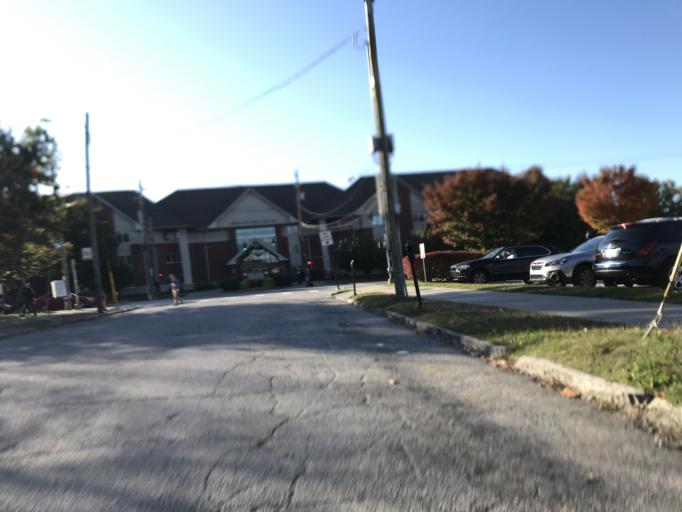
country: US
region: Kentucky
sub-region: Jefferson County
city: Louisville
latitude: 38.2195
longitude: -85.7625
